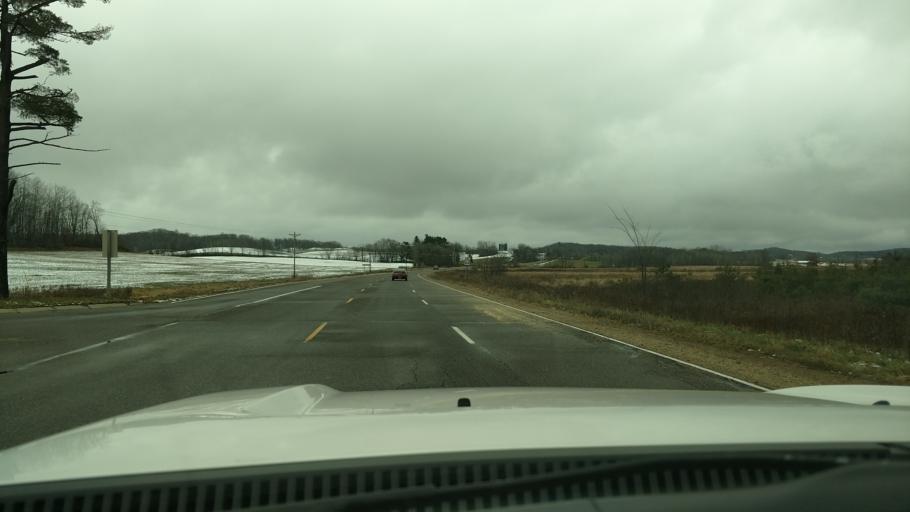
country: US
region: Wisconsin
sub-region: Dunn County
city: Boyceville
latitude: 45.1400
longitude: -91.9703
